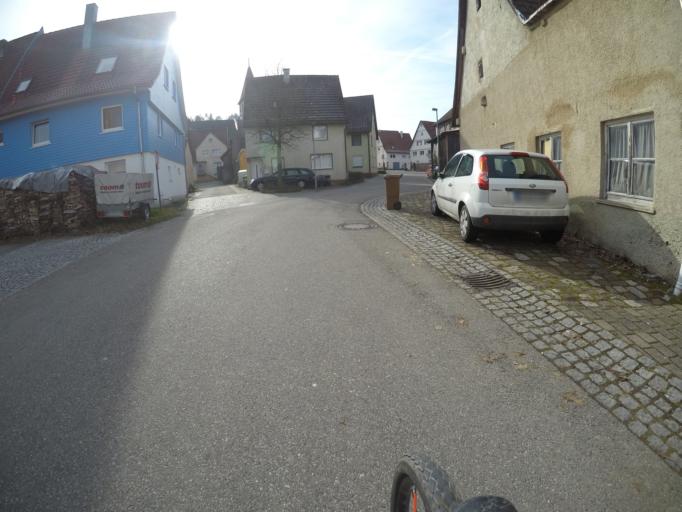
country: DE
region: Baden-Wuerttemberg
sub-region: Karlsruhe Region
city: Wildberg
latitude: 48.6491
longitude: 8.7763
